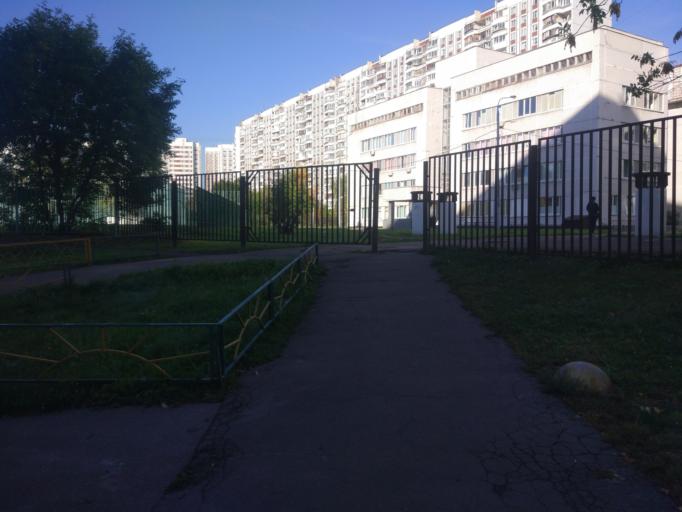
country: RU
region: Moskovskaya
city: Reutov
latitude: 55.7423
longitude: 37.8763
